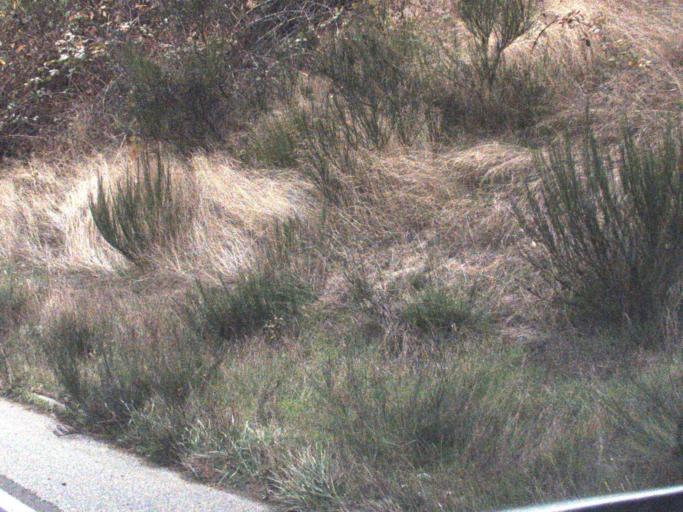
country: US
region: Washington
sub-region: Island County
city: Langley
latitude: 47.9793
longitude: -122.3701
